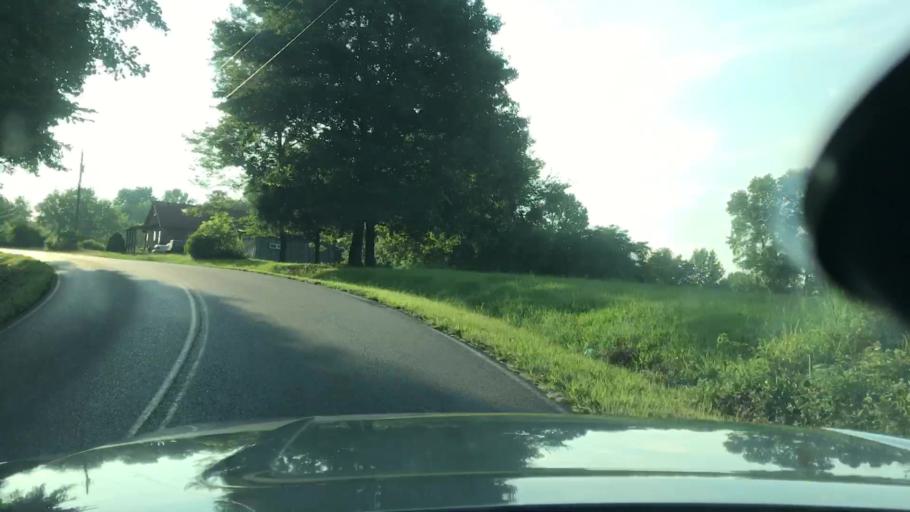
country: US
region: Tennessee
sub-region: Sumner County
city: Gallatin
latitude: 36.4820
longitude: -86.4400
